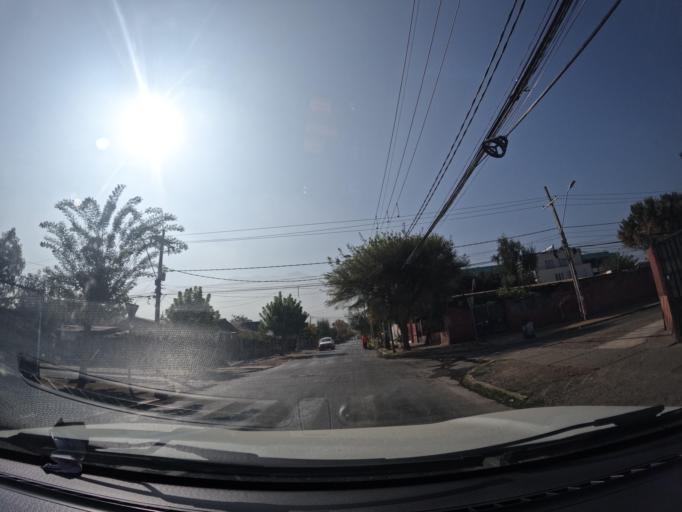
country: CL
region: Santiago Metropolitan
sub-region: Provincia de Santiago
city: Villa Presidente Frei, Nunoa, Santiago, Chile
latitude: -33.4727
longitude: -70.5473
